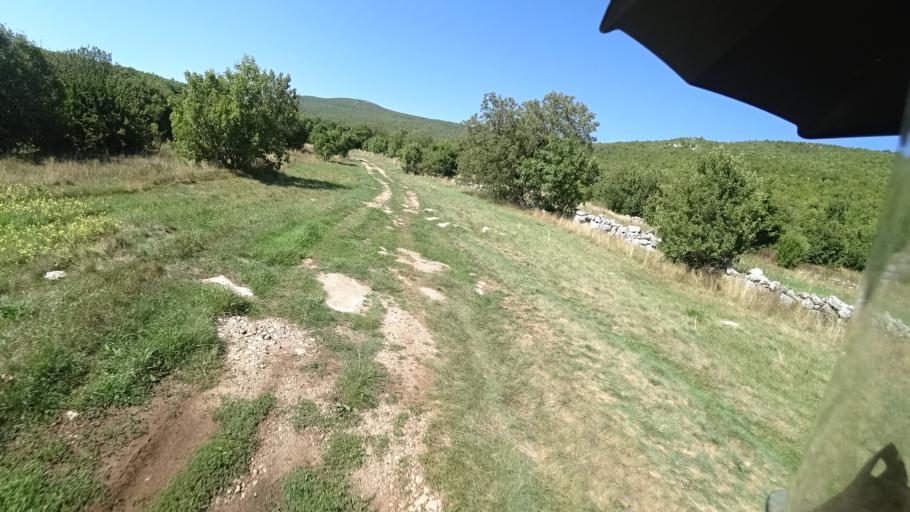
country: HR
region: Splitsko-Dalmatinska
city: Hrvace
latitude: 43.8866
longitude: 16.5712
